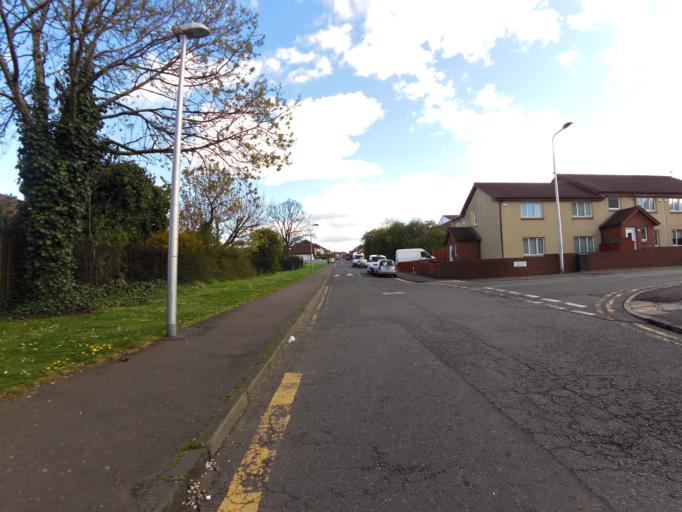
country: GB
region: Scotland
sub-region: Midlothian
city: Loanhead
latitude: 55.9173
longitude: -3.1364
